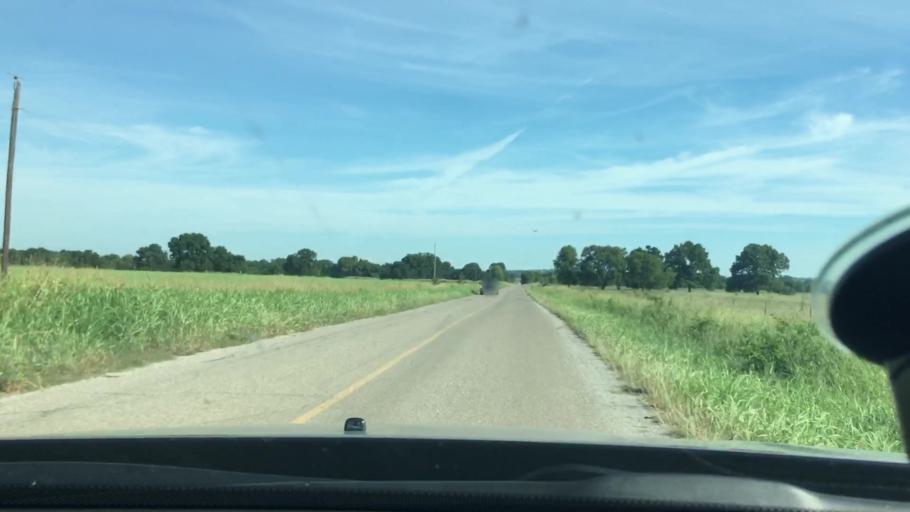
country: US
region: Oklahoma
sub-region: Carter County
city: Lone Grove
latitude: 34.2974
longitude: -97.2824
